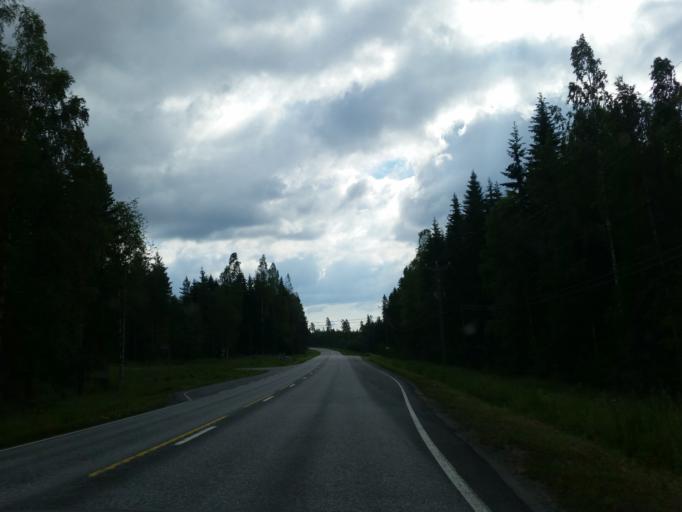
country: FI
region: Northern Savo
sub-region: Kuopio
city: Kuopio
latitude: 62.8417
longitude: 27.4905
